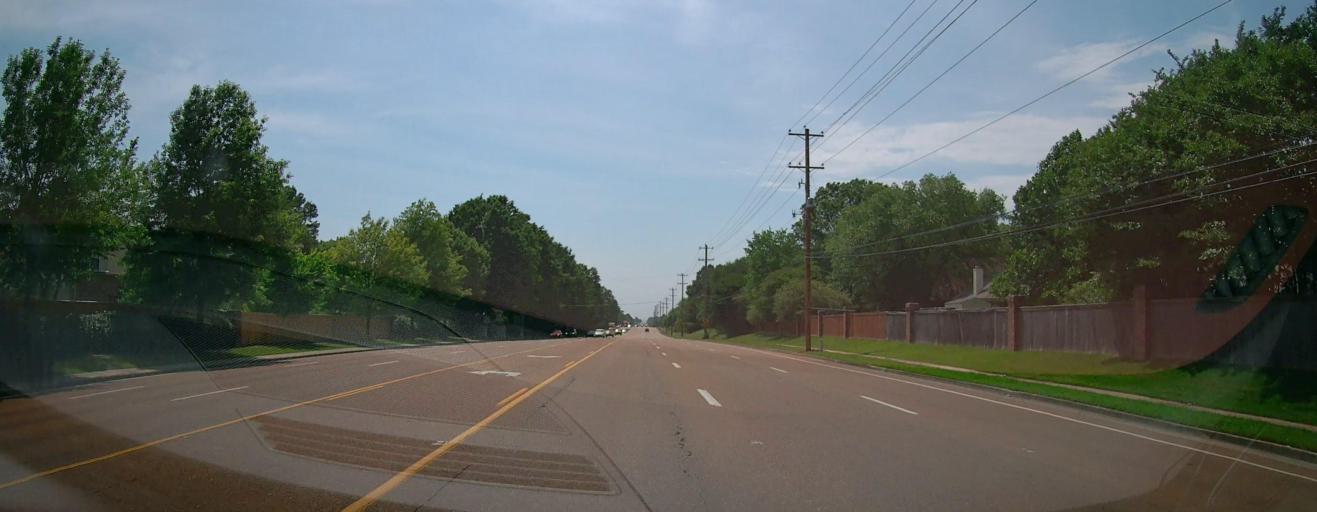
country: US
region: Mississippi
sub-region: De Soto County
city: Olive Branch
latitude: 35.0205
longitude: -89.8143
